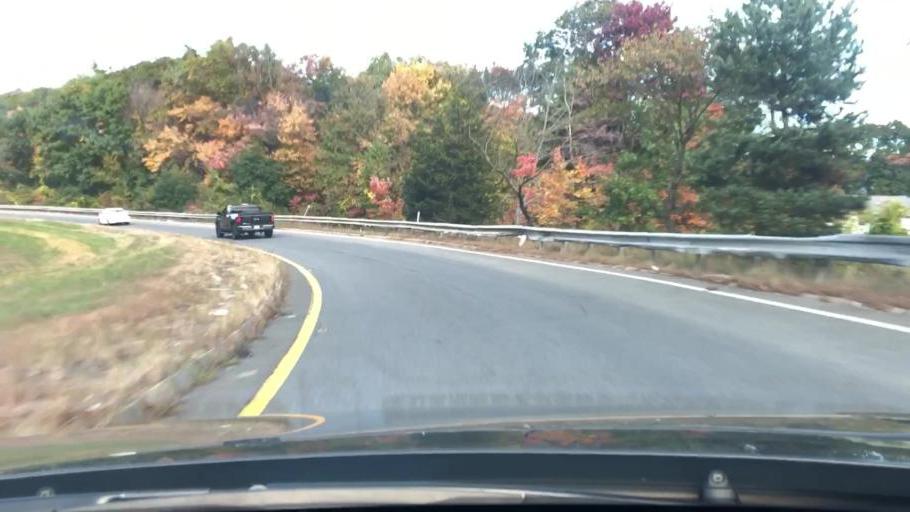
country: US
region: Massachusetts
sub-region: Essex County
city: Lawrence
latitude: 42.7399
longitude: -71.1397
